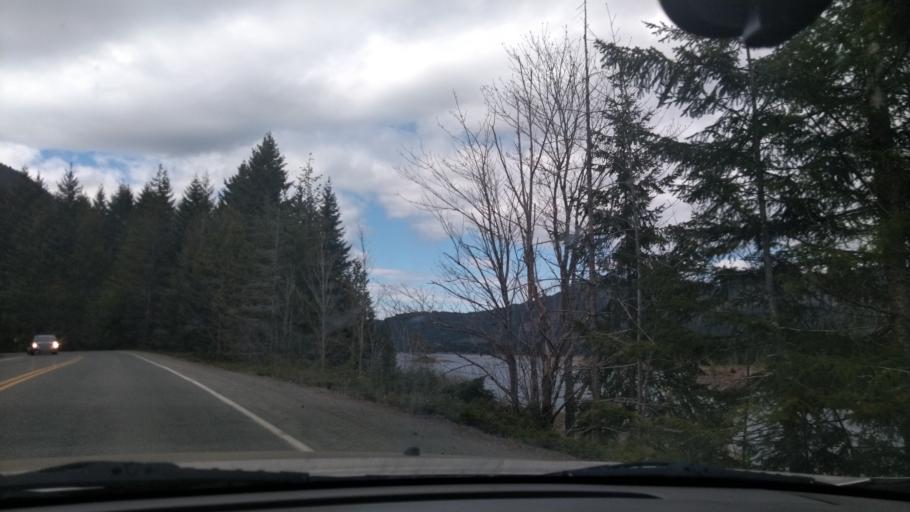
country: CA
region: British Columbia
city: Campbell River
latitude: 49.8467
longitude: -125.6421
